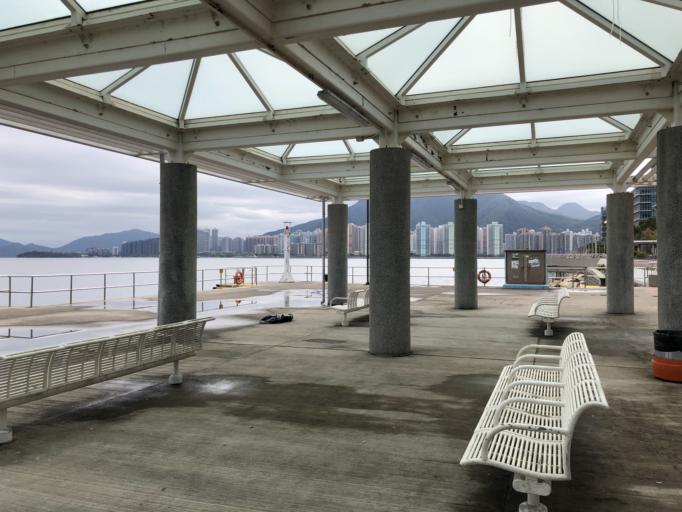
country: HK
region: Tai Po
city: Tai Po
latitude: 22.4303
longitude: 114.2086
